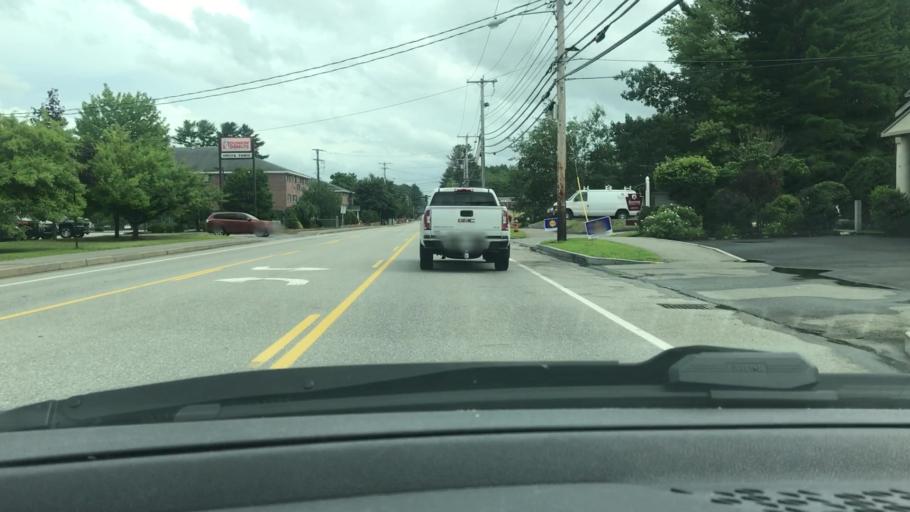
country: US
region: New Hampshire
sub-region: Merrimack County
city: East Concord
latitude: 43.2583
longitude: -71.5798
